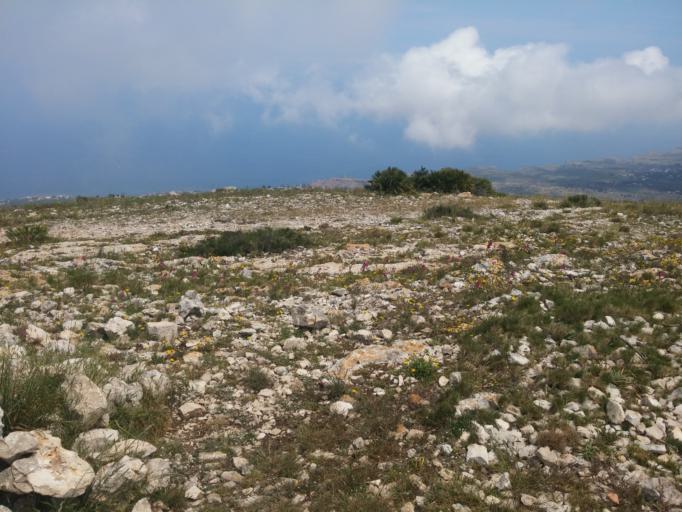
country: ES
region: Valencia
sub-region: Provincia de Alicante
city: Javea
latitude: 38.8032
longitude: 0.1294
